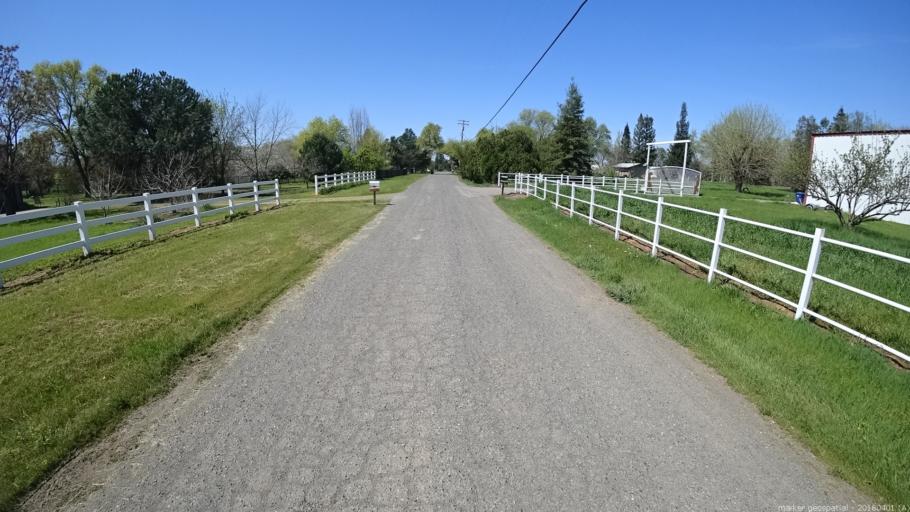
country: US
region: California
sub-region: Sacramento County
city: Wilton
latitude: 38.4492
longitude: -121.1833
